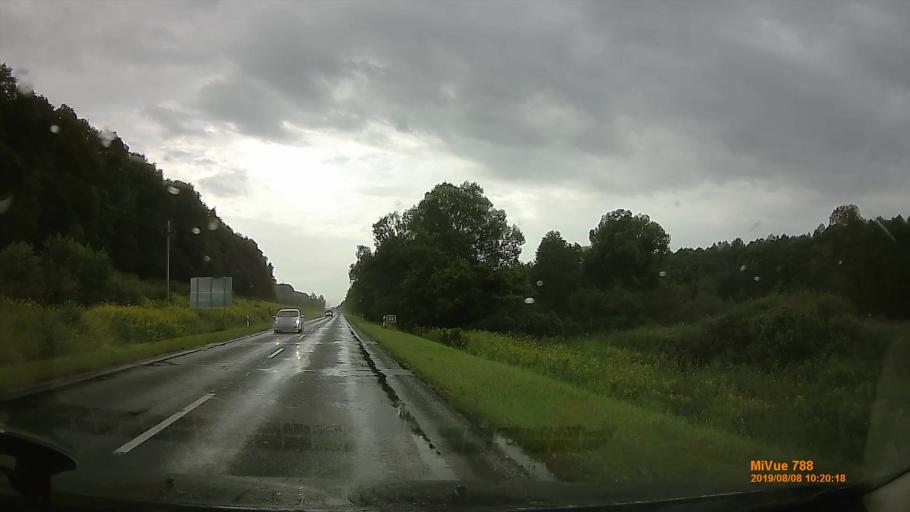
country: HU
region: Zala
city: Zalaegerszeg
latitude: 46.7534
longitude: 16.8571
